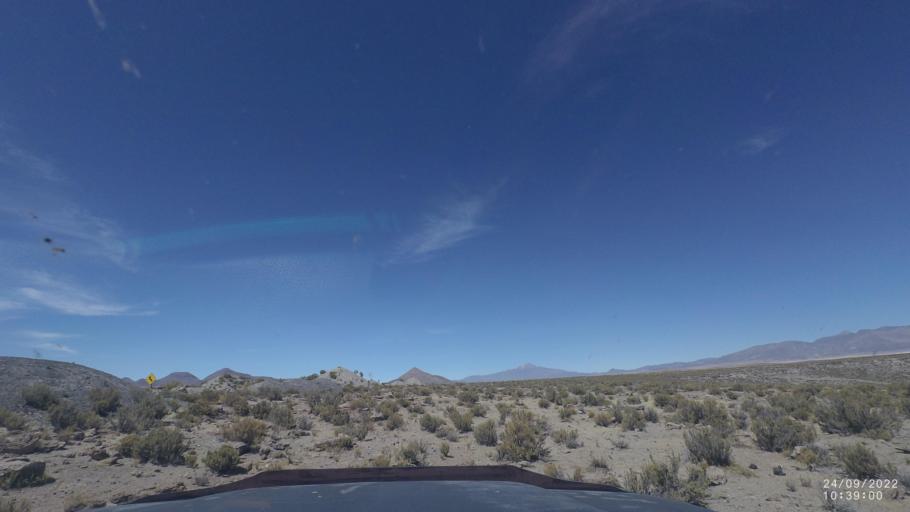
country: BO
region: Oruro
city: Challapata
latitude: -19.4673
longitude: -67.4275
